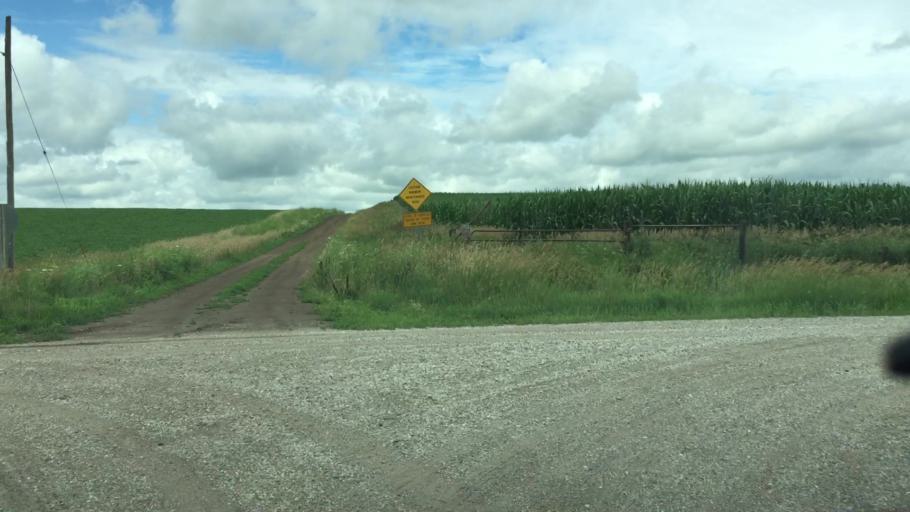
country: US
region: Iowa
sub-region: Jasper County
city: Monroe
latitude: 41.5662
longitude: -93.1207
